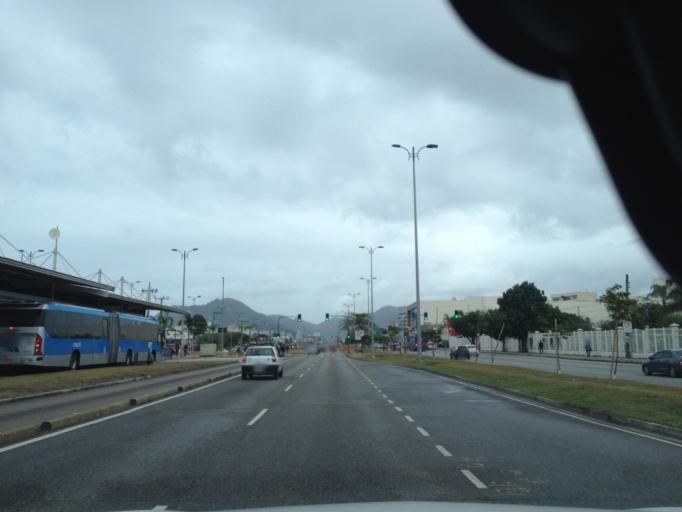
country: BR
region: Rio de Janeiro
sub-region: Nilopolis
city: Nilopolis
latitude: -23.0121
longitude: -43.4584
